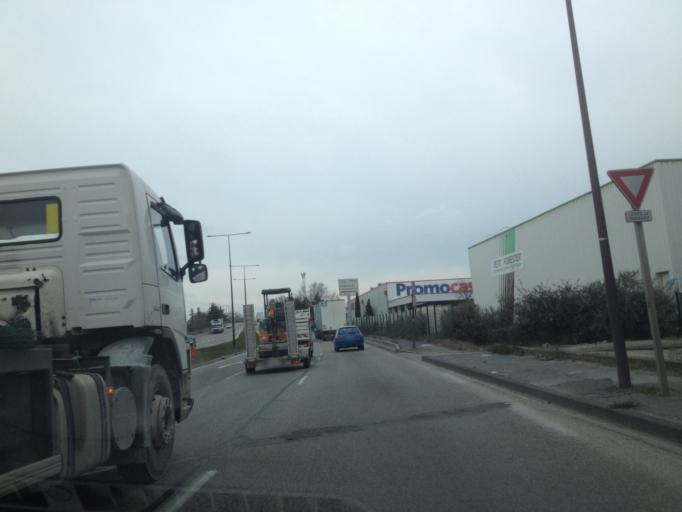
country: FR
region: Provence-Alpes-Cote d'Azur
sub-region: Departement du Vaucluse
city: Avignon
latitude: 43.9345
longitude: 4.8321
